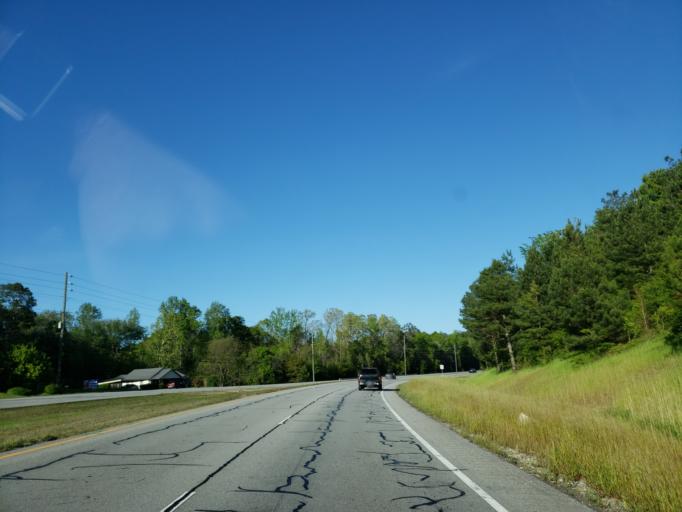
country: US
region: Georgia
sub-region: Paulding County
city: Dallas
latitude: 33.9181
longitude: -84.8753
